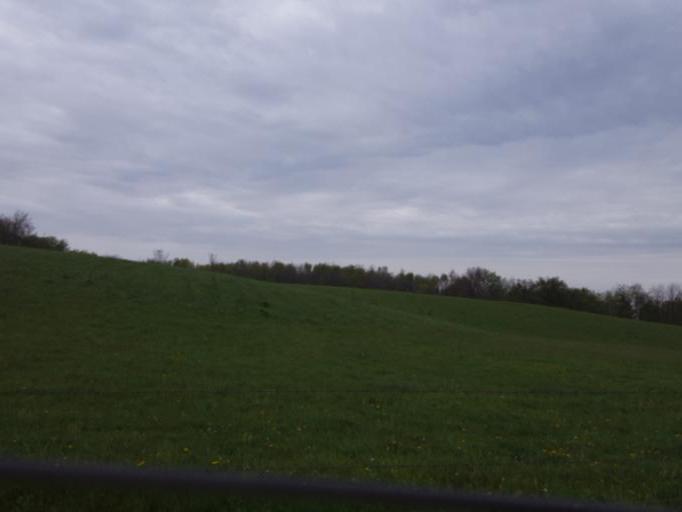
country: US
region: Ohio
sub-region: Richland County
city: Lexington
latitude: 40.7008
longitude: -82.6454
